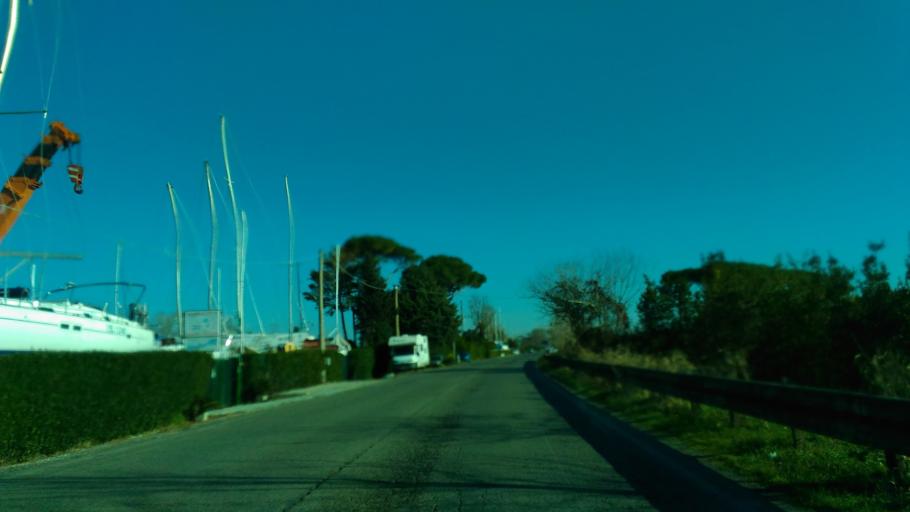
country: IT
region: Tuscany
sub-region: Province of Pisa
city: Marina di Pisa
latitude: 43.6765
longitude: 10.3101
